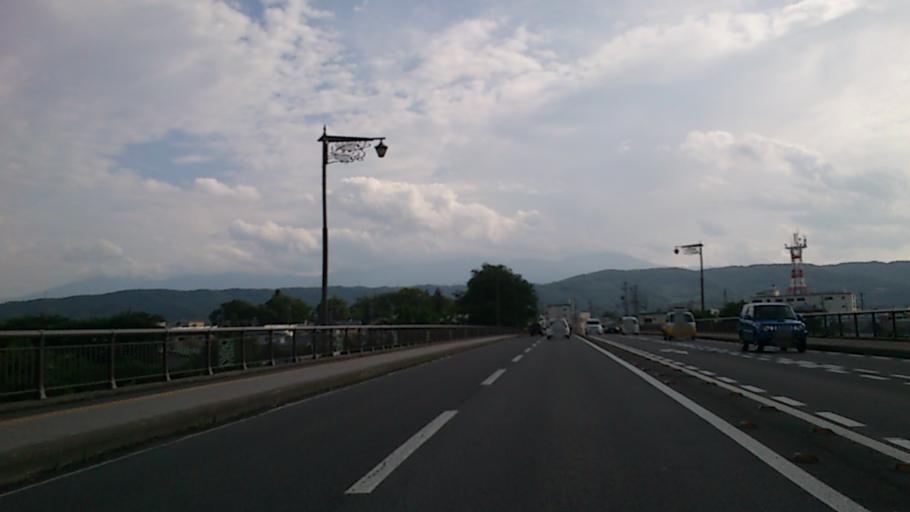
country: JP
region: Nagano
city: Saku
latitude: 36.2296
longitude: 138.4731
